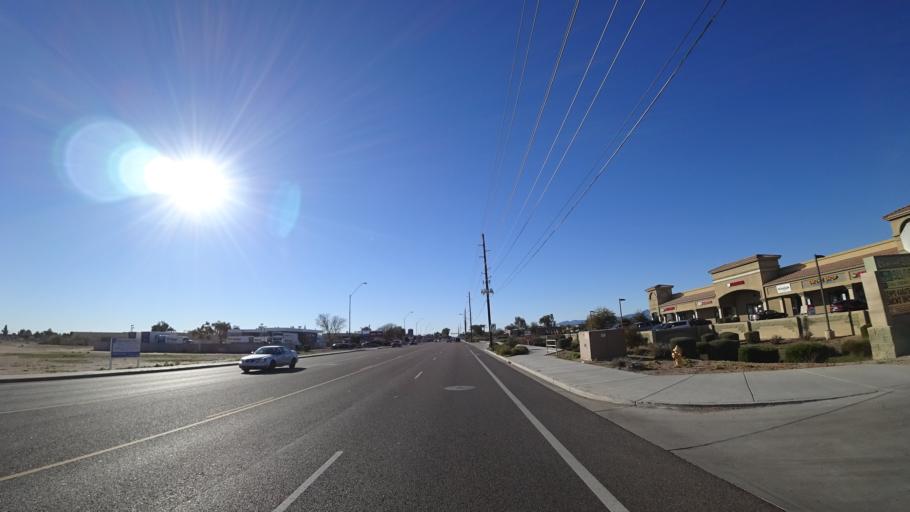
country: US
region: Arizona
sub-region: Maricopa County
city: Avondale
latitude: 33.4499
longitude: -112.3464
